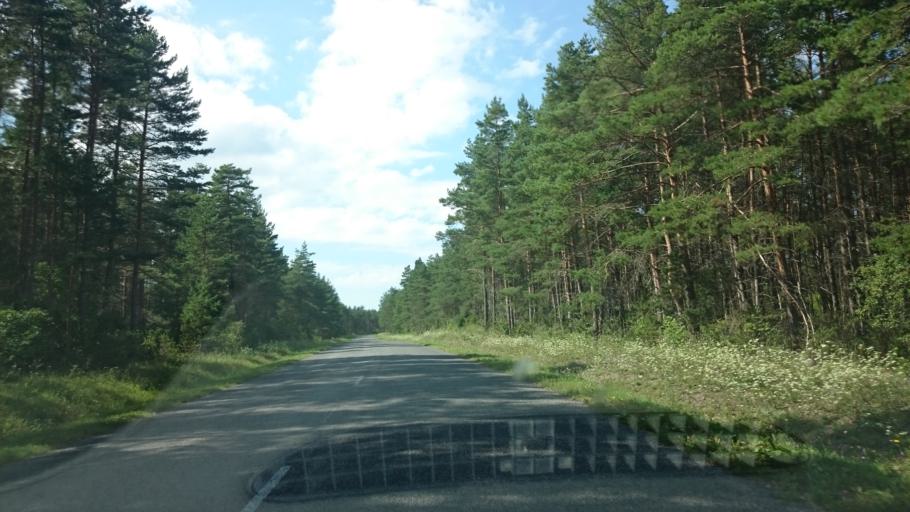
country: EE
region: Saare
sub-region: Orissaare vald
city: Orissaare
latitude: 58.5908
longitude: 23.0137
